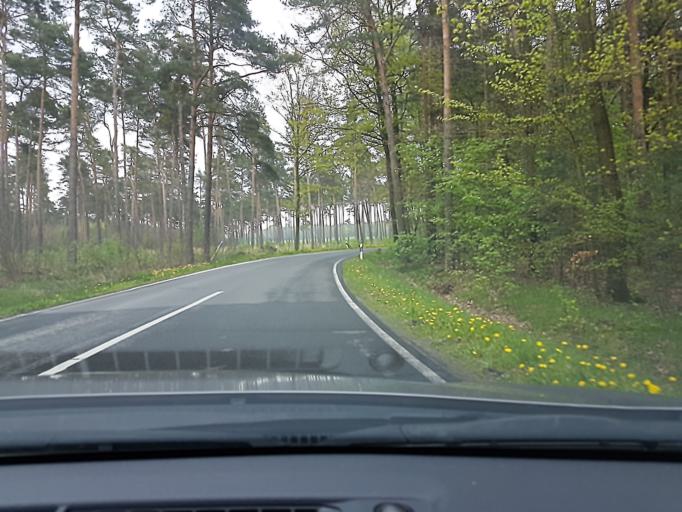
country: DE
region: Saxony
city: Schildau
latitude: 51.4675
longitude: 12.9782
